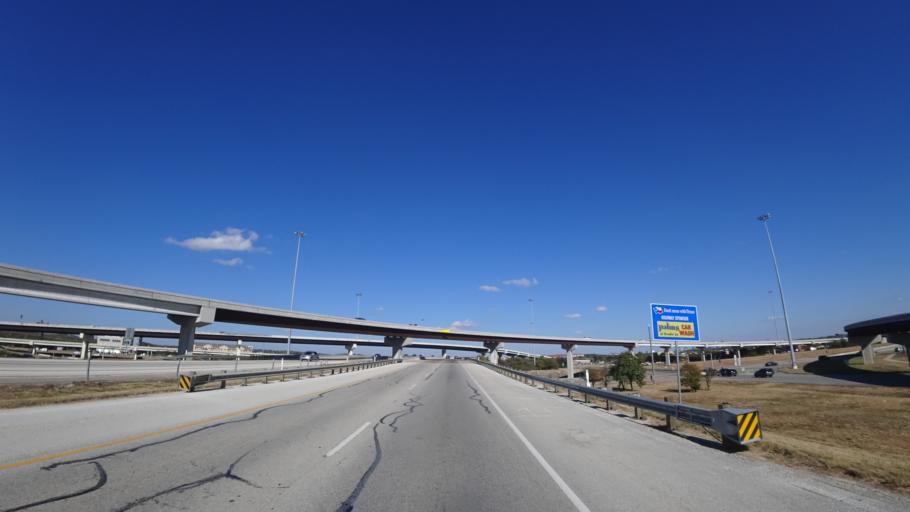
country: US
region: Texas
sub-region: Travis County
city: Rollingwood
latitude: 30.2339
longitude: -97.8254
